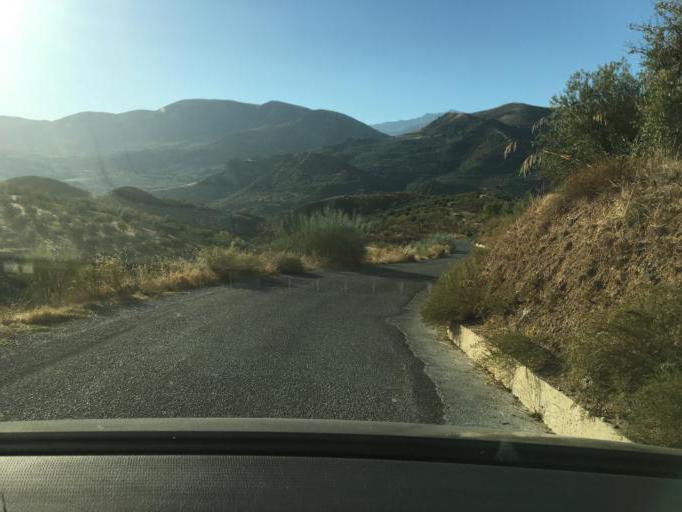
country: ES
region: Andalusia
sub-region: Provincia de Granada
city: Quentar
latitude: 37.2017
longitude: -3.4708
